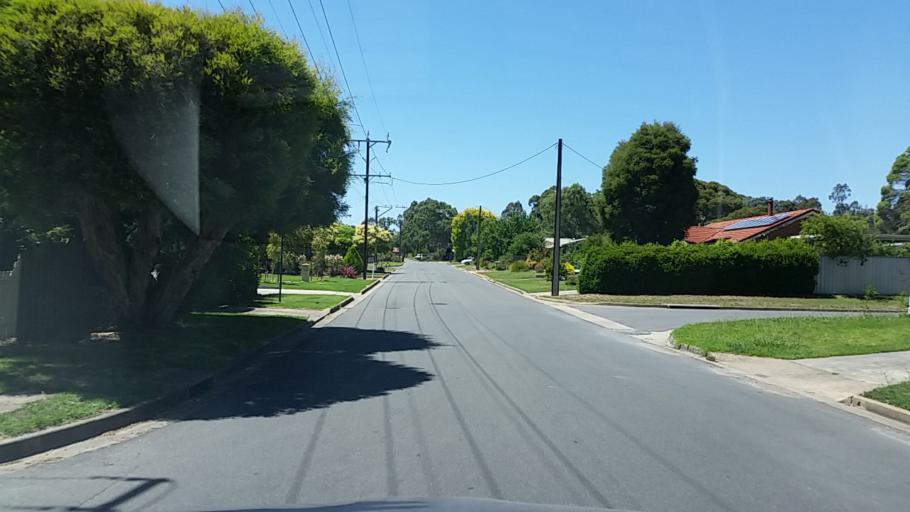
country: AU
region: South Australia
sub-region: Adelaide Hills
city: Balhannah
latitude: -34.9929
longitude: 138.8297
